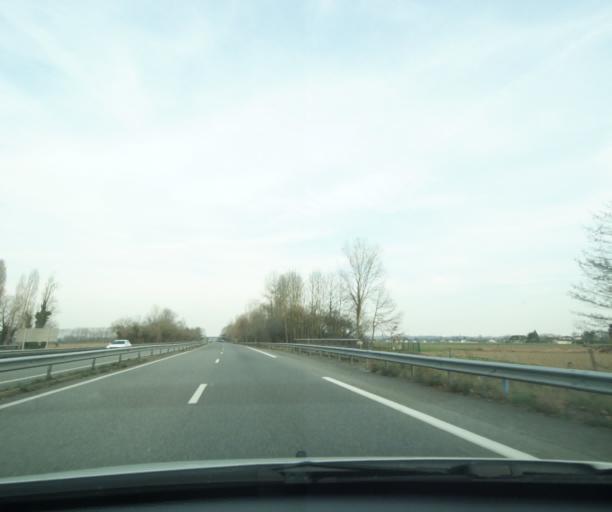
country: FR
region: Midi-Pyrenees
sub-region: Departement des Hautes-Pyrenees
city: Odos
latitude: 43.2090
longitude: 0.0530
